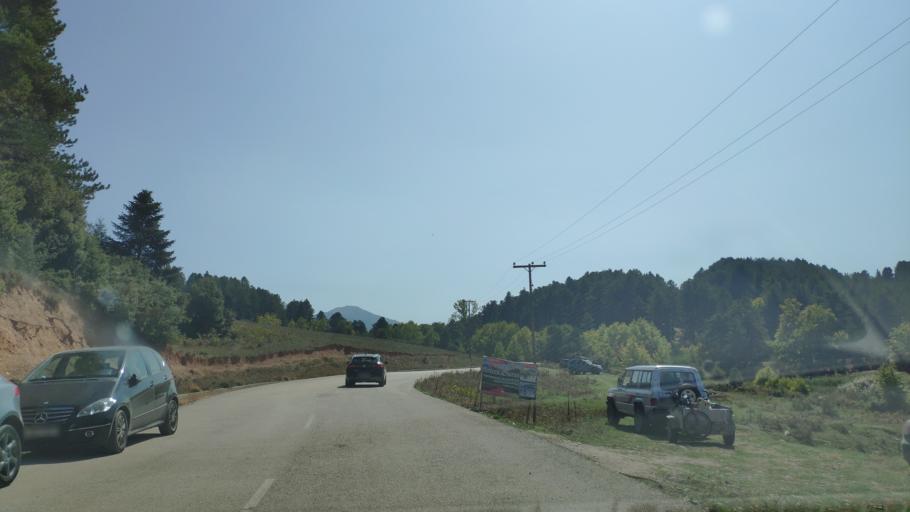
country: GR
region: West Greece
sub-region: Nomos Achaias
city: Kalavryta
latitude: 37.9261
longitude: 22.2925
